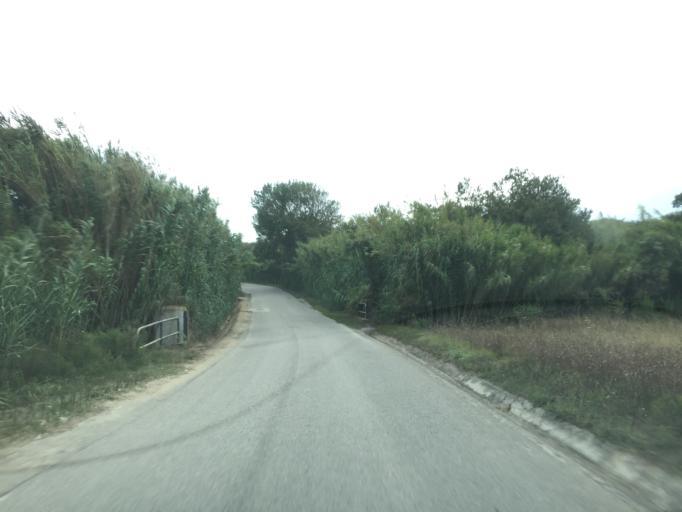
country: PT
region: Leiria
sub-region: Peniche
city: Atouguia da Baleia
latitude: 39.3482
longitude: -9.2963
